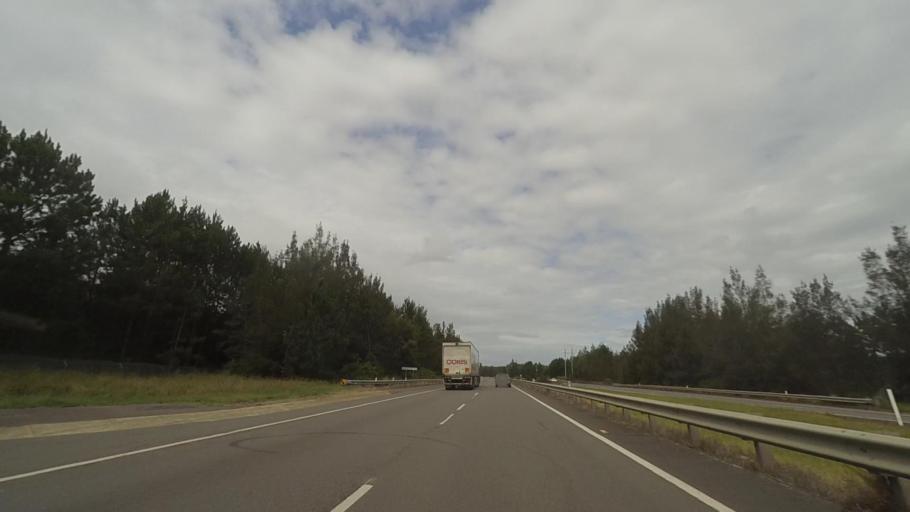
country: AU
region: New South Wales
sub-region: Port Stephens Shire
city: Raymond Terrace
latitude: -32.7790
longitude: 151.7487
